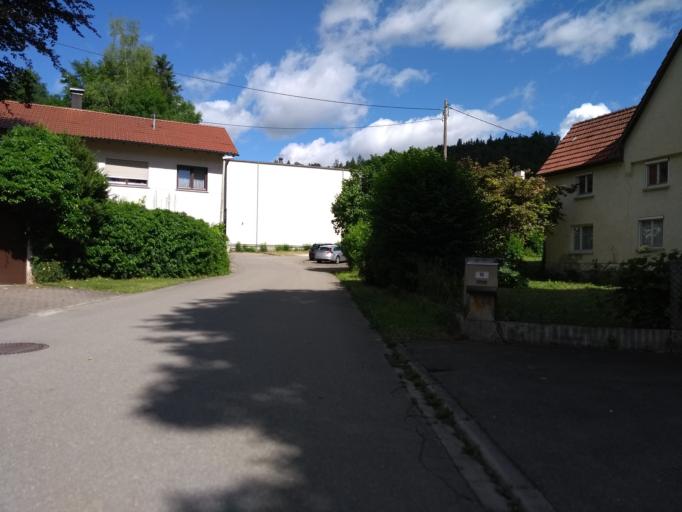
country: DE
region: Baden-Wuerttemberg
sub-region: Tuebingen Region
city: Schelklingen
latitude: 48.3645
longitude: 9.7122
